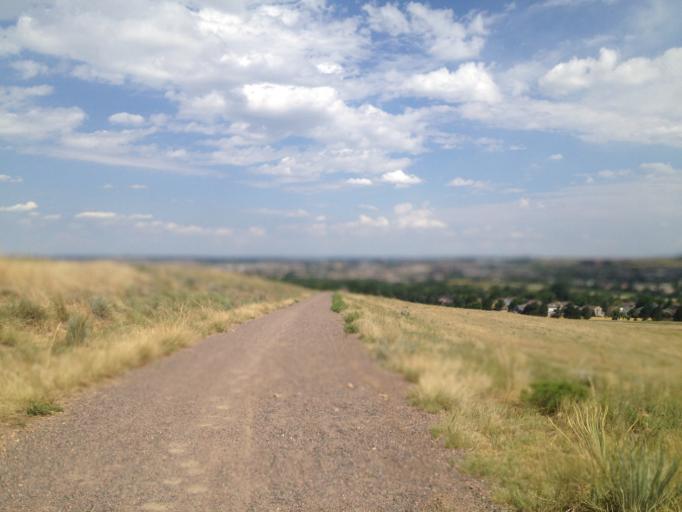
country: US
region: Colorado
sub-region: Boulder County
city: Superior
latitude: 39.9351
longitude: -105.1695
